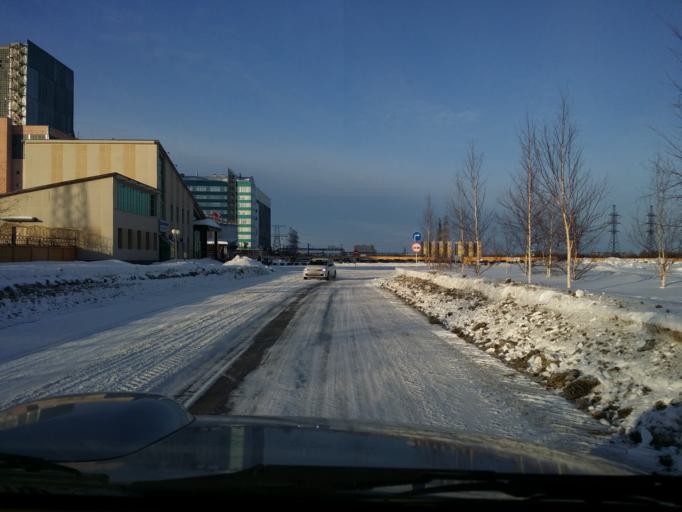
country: RU
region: Khanty-Mansiyskiy Avtonomnyy Okrug
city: Izluchinsk
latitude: 60.9735
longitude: 76.9455
